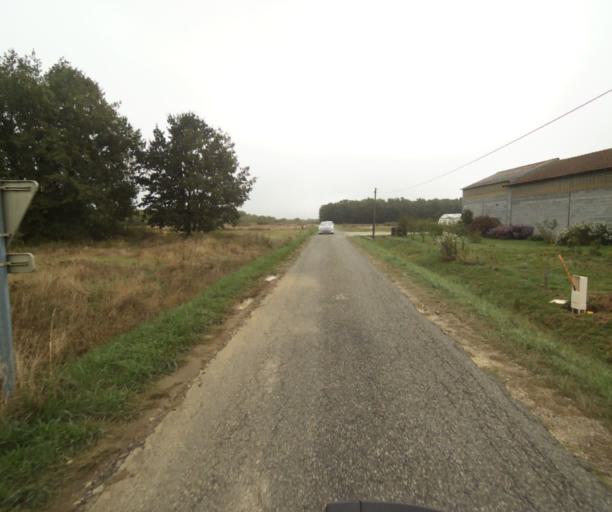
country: FR
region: Midi-Pyrenees
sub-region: Departement du Tarn-et-Garonne
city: Orgueil
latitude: 43.9045
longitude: 1.3867
